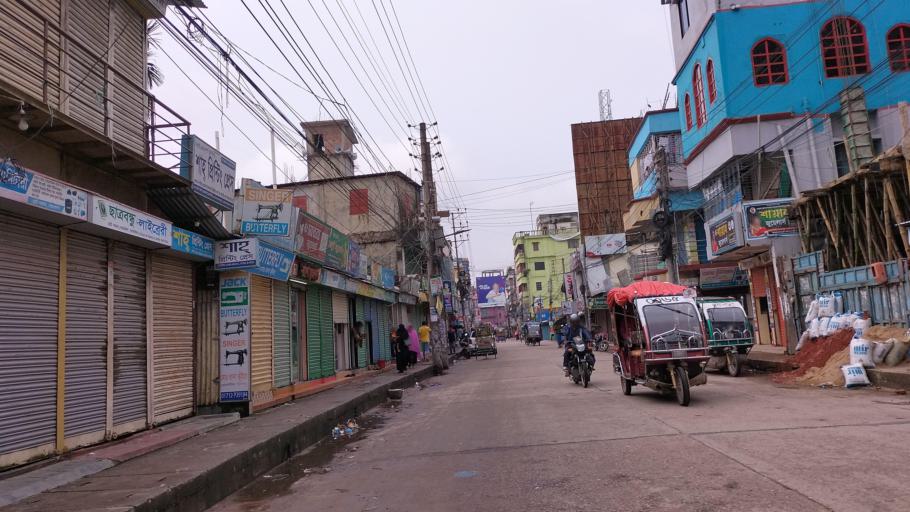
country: BD
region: Dhaka
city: Netrakona
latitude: 24.8822
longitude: 90.7322
